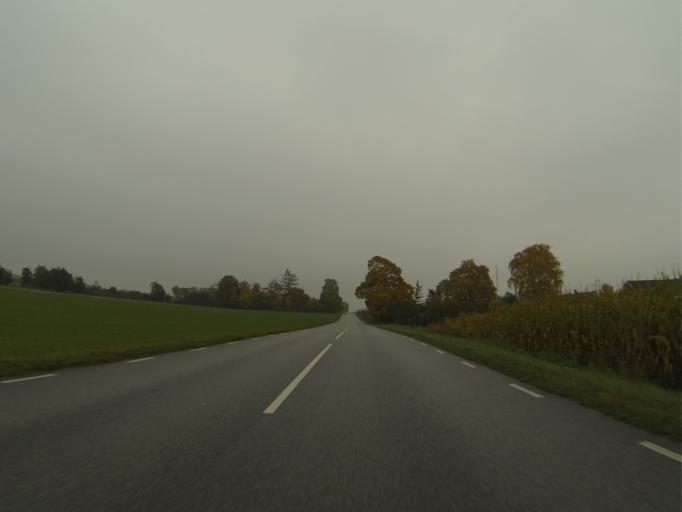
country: SE
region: Skane
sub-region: Hoors Kommun
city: Loberod
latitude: 55.7130
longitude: 13.5386
